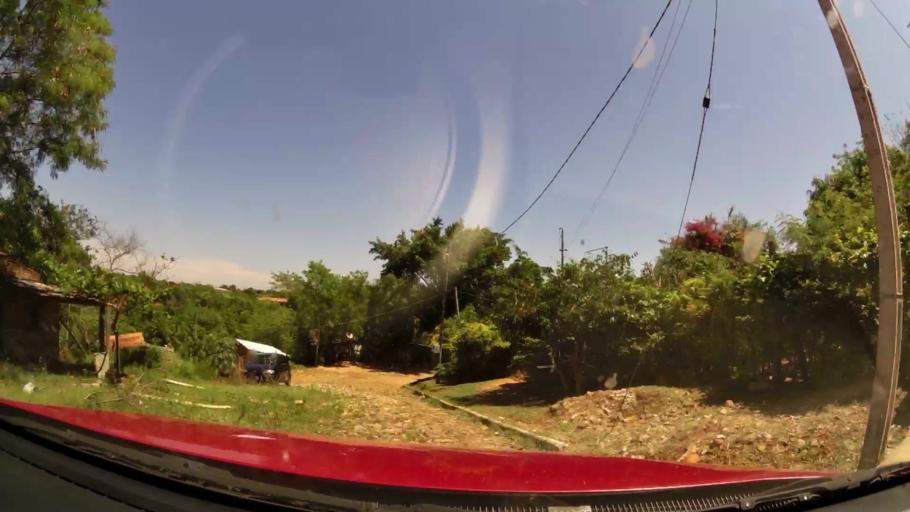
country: PY
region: Central
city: Colonia Mariano Roque Alonso
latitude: -25.2368
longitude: -57.5519
